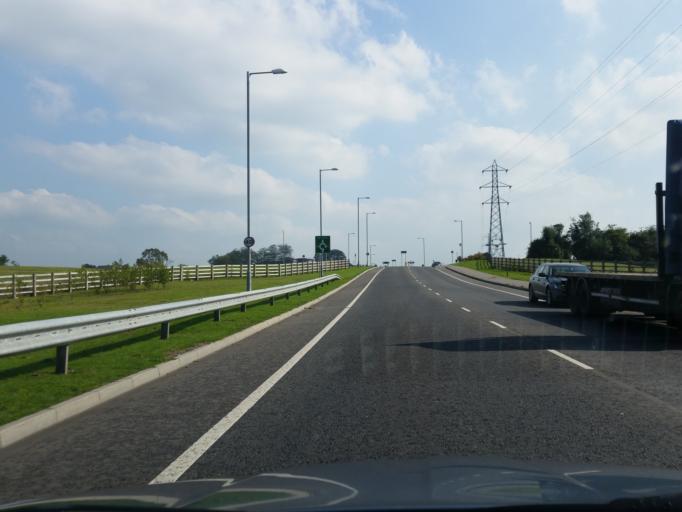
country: GB
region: Northern Ireland
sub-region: Fermanagh District
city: Enniskillen
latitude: 54.3583
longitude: -7.6239
